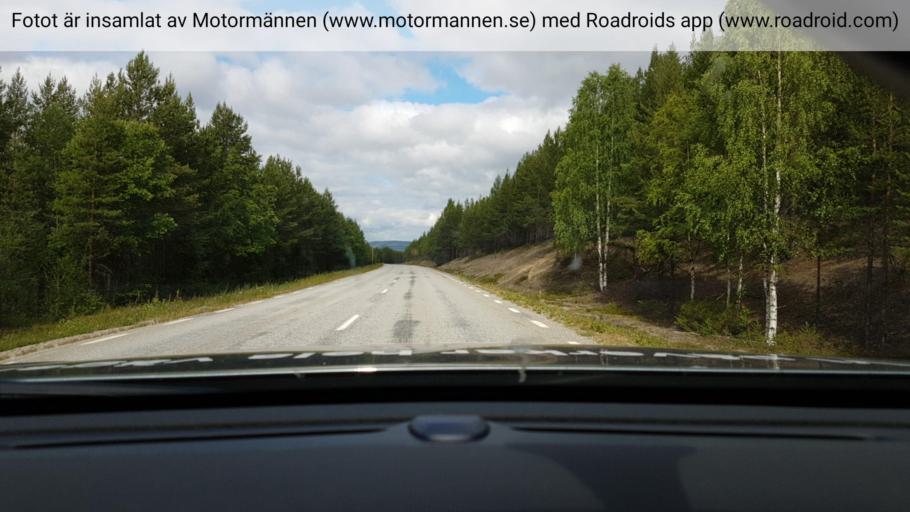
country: SE
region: Vaesterbotten
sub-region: Mala Kommun
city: Mala
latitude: 64.9160
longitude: 18.6436
